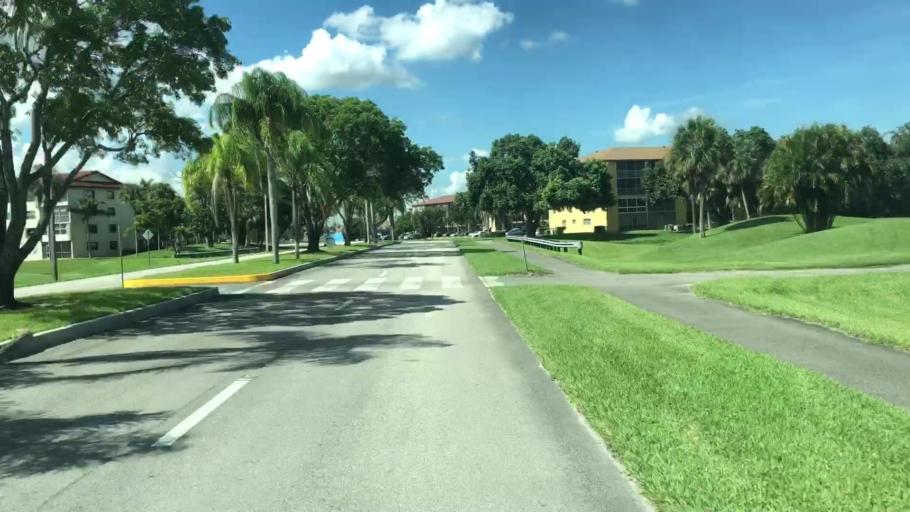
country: US
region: Florida
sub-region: Broward County
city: Sunshine Ranches
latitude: 26.0026
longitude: -80.3213
